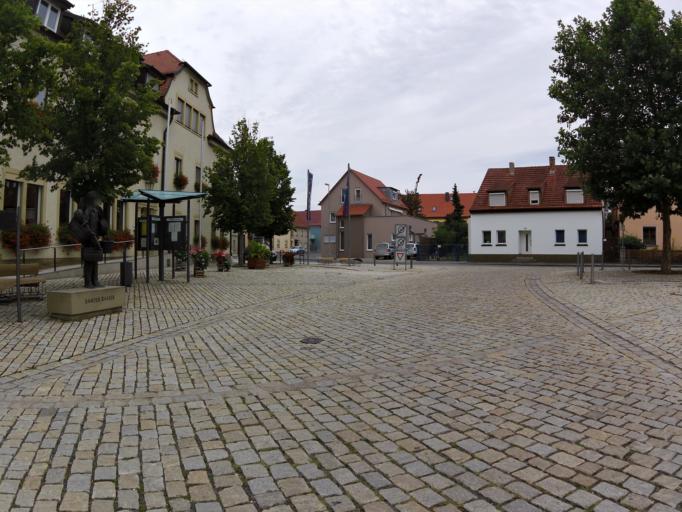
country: DE
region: Bavaria
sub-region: Regierungsbezirk Unterfranken
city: Sand
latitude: 49.9888
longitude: 10.5880
